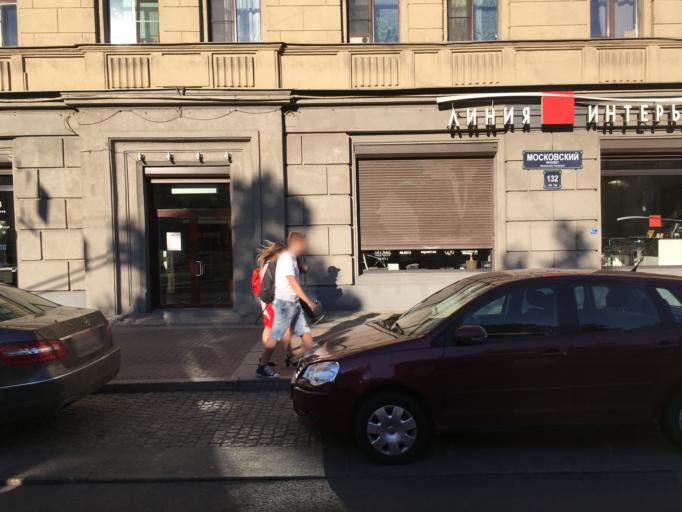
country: RU
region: St.-Petersburg
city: Admiralteisky
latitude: 59.8879
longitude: 30.3201
